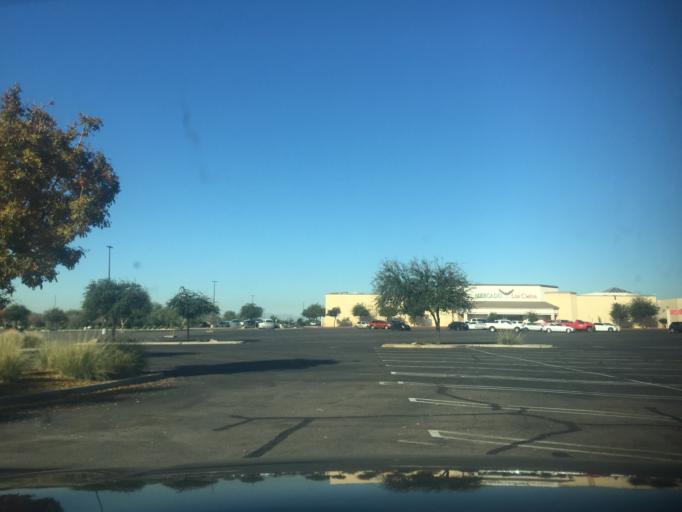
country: US
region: Arizona
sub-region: Maricopa County
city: Tolleson
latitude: 33.4746
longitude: -112.2226
